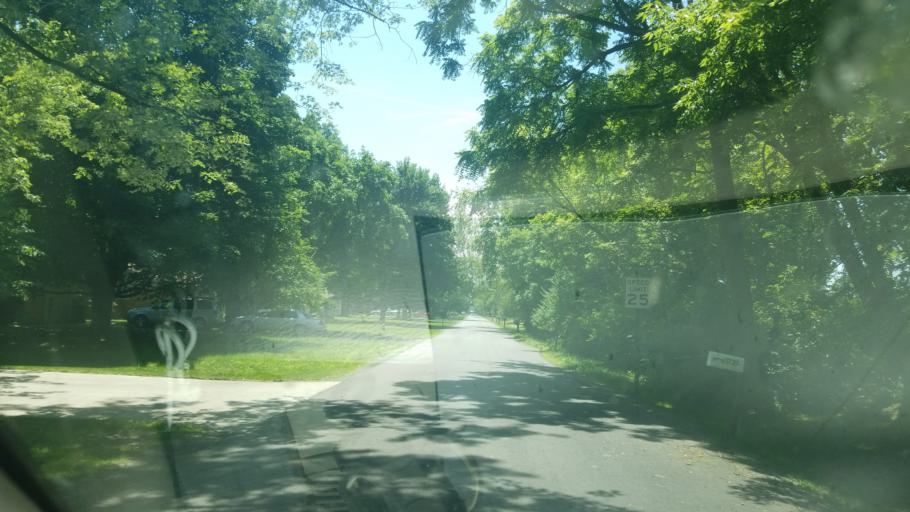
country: US
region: Ohio
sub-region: Hancock County
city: Findlay
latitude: 41.0188
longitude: -83.6348
